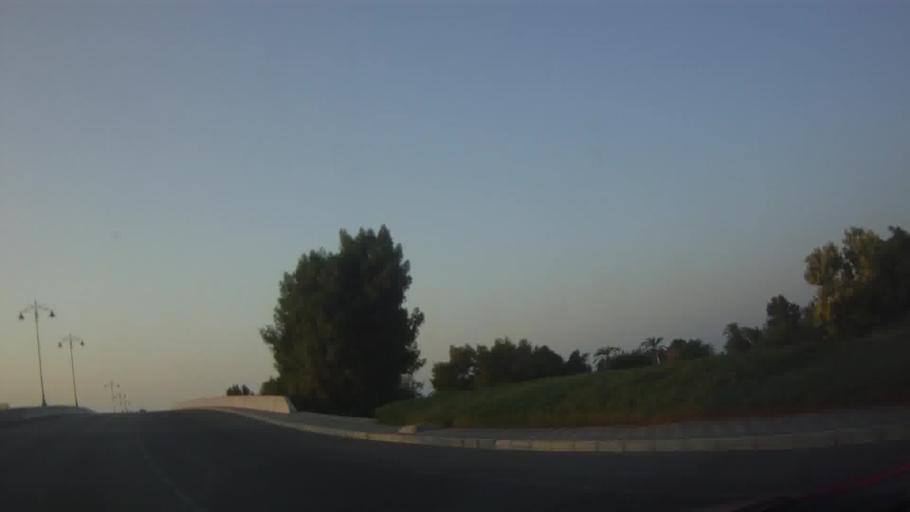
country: OM
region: Muhafazat Masqat
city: Bawshar
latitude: 23.6123
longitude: 58.4738
